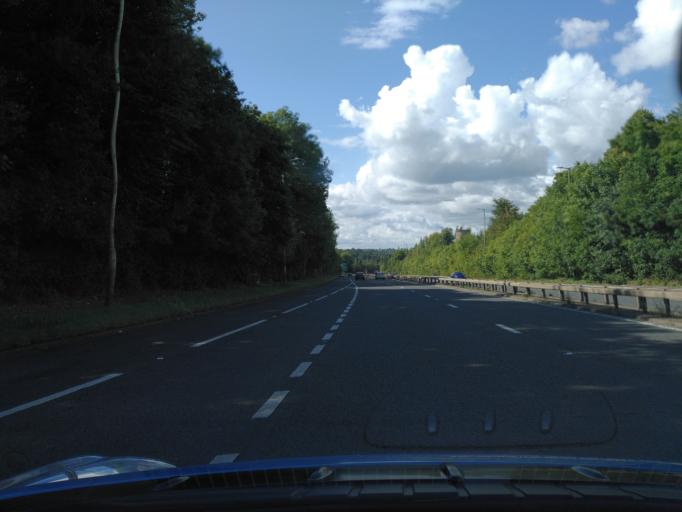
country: GB
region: England
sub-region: Hertfordshire
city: Abbots Langley
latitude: 51.6850
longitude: -0.4199
